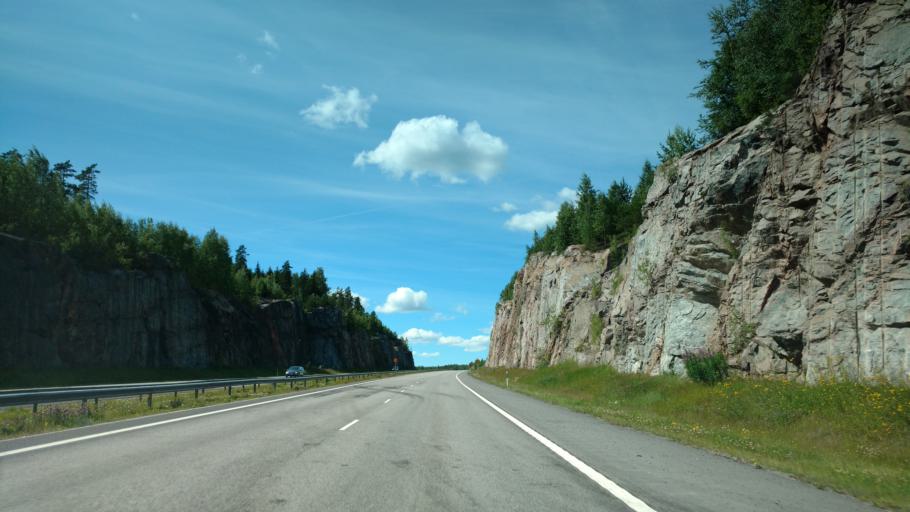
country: FI
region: Varsinais-Suomi
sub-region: Salo
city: Halikko
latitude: 60.4314
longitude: 22.9974
